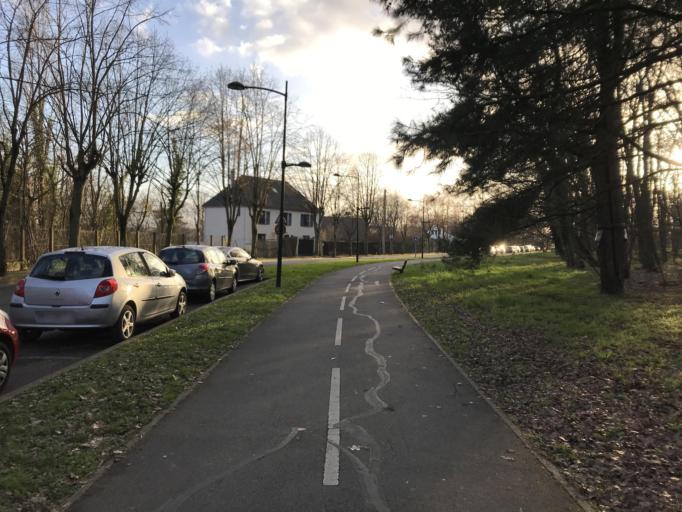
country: FR
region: Ile-de-France
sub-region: Departement de l'Essonne
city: Villebon-sur-Yvette
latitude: 48.7140
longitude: 2.2365
